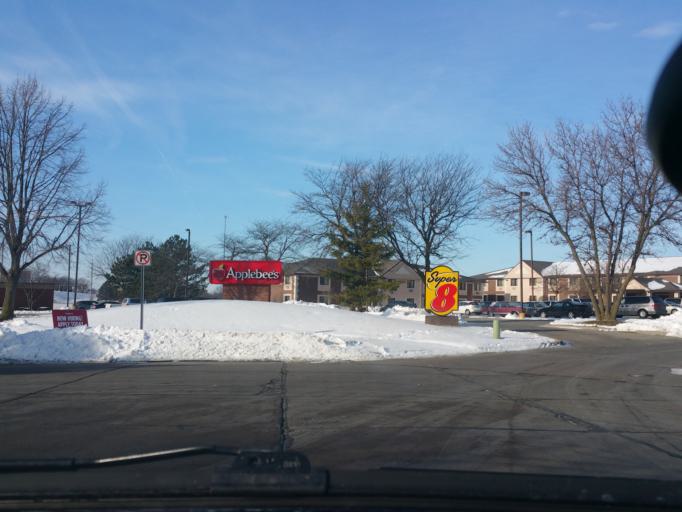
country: US
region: Iowa
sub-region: Polk County
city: Clive
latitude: 41.6016
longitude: -93.7737
